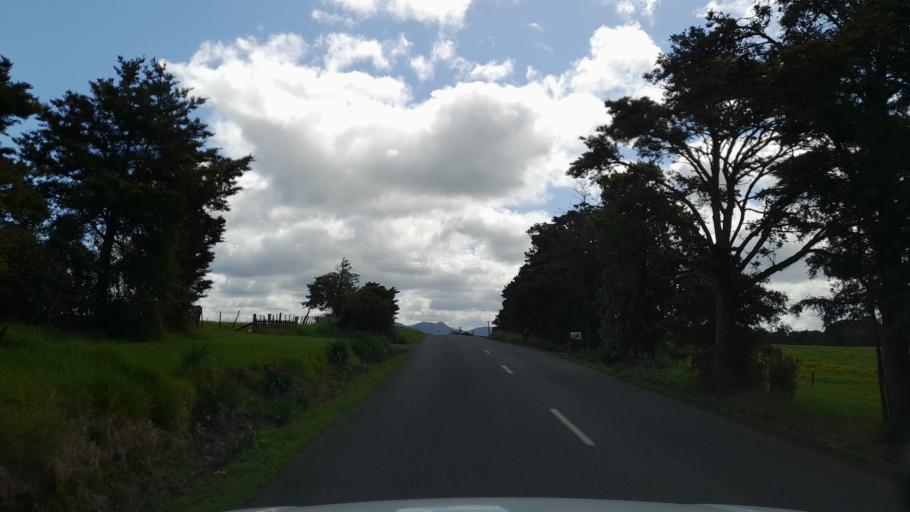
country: NZ
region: Northland
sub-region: Whangarei
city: Maungatapere
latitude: -35.7077
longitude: 174.0495
